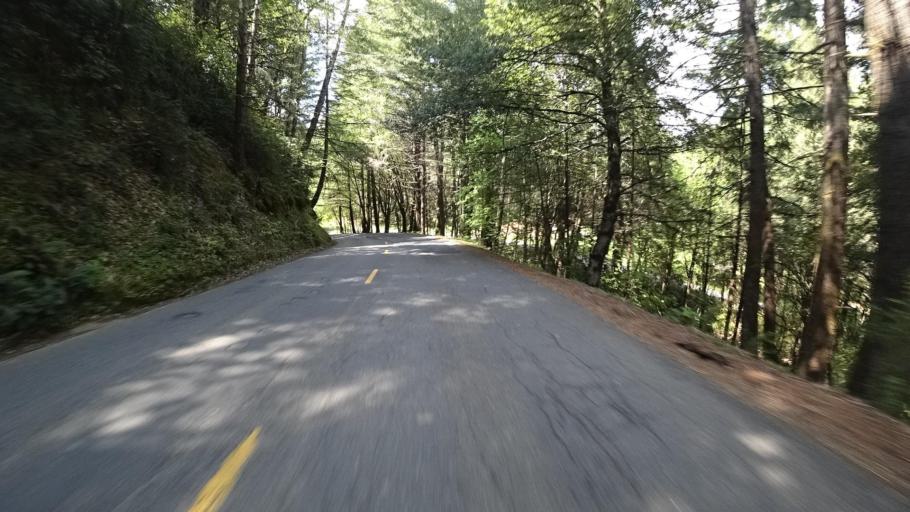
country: US
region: California
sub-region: Humboldt County
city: Redway
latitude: 40.0910
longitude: -123.9377
